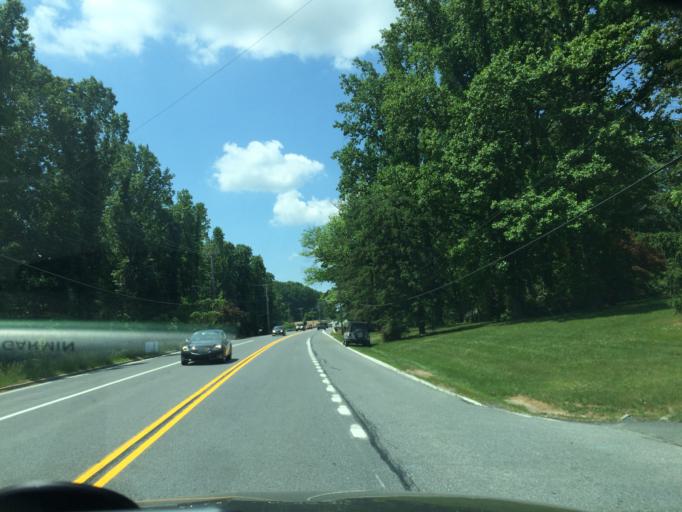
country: US
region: Maryland
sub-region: Carroll County
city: Eldersburg
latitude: 39.4238
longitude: -76.9381
